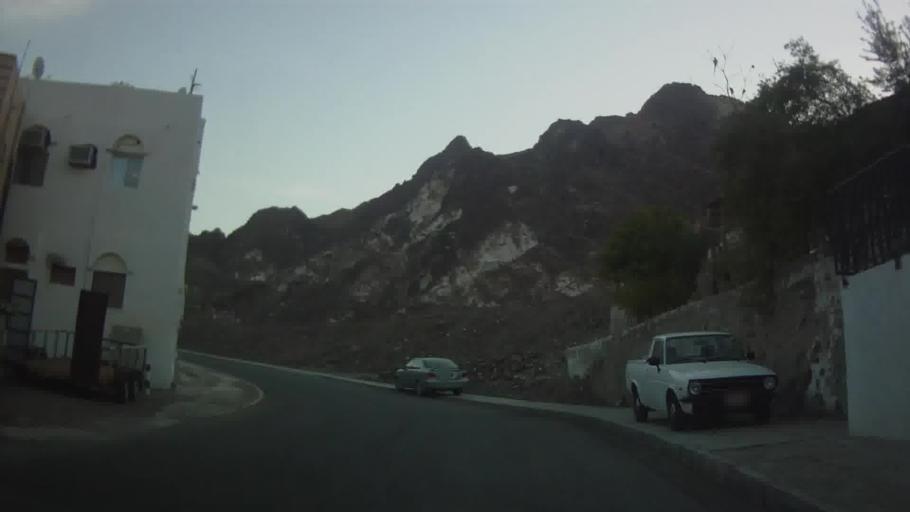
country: OM
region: Muhafazat Masqat
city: Muscat
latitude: 23.6169
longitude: 58.5857
